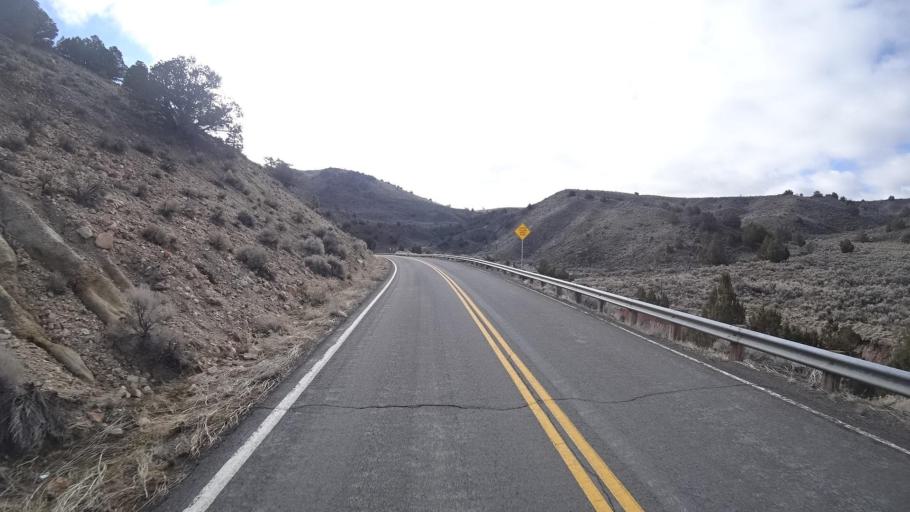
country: US
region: Nevada
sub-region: Washoe County
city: Cold Springs
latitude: 39.9037
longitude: -119.9987
